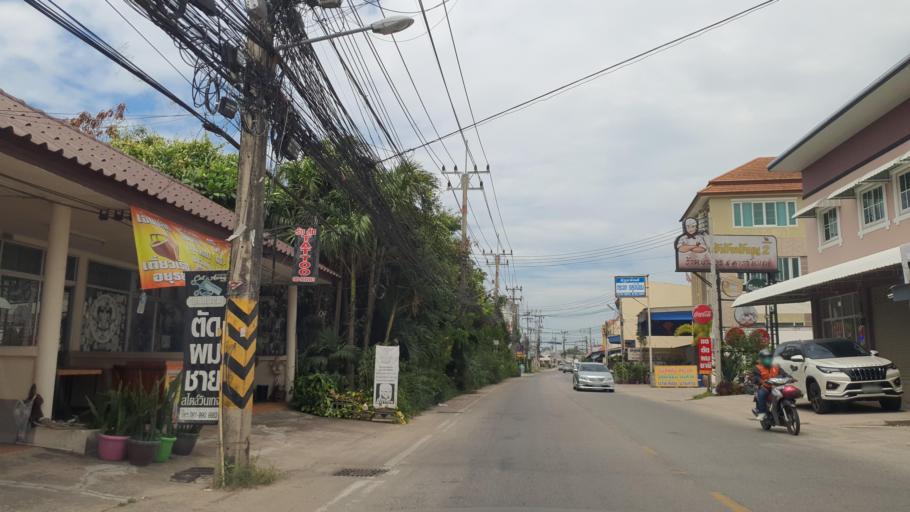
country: TH
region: Chon Buri
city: Bang Lamung
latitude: 12.9823
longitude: 100.9315
